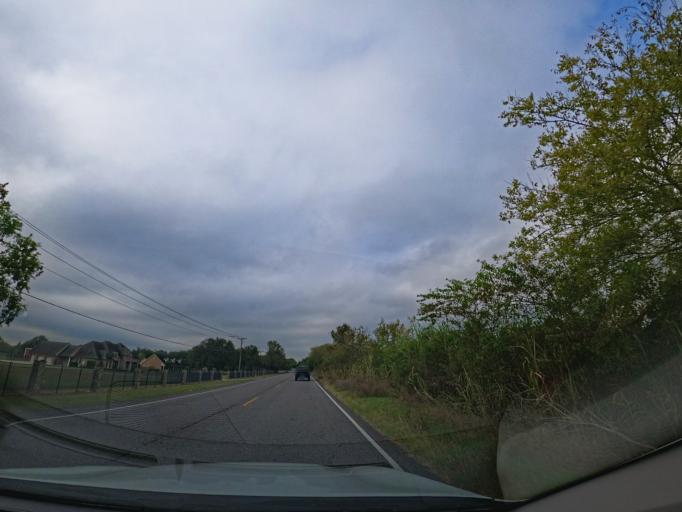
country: US
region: Louisiana
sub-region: Terrebonne Parish
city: Houma
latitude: 29.5719
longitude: -90.7644
